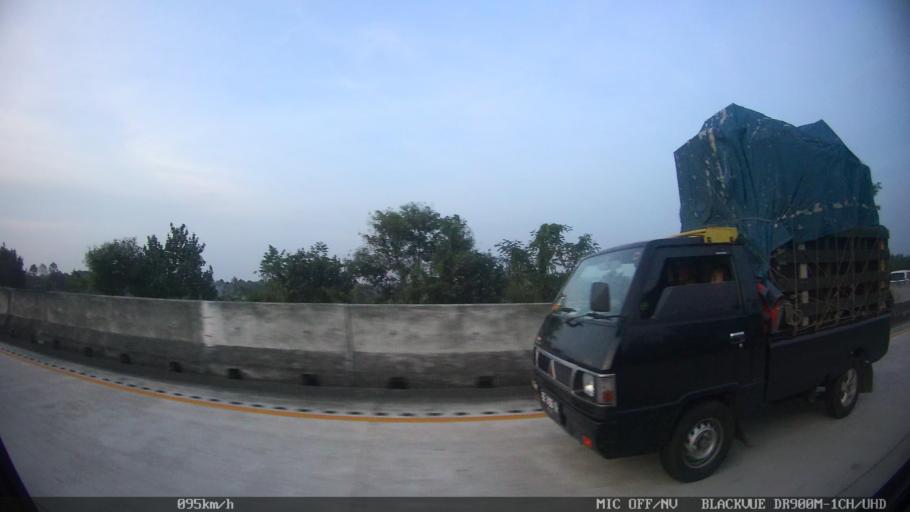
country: ID
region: Lampung
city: Pasuruan
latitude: -5.7305
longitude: 105.6750
